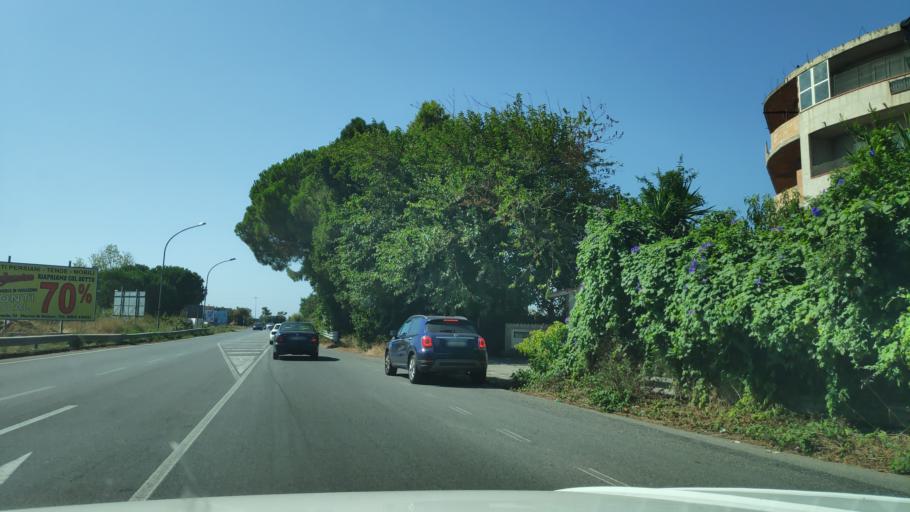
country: IT
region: Calabria
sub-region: Provincia di Reggio Calabria
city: Bovalino
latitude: 38.1402
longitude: 16.1655
